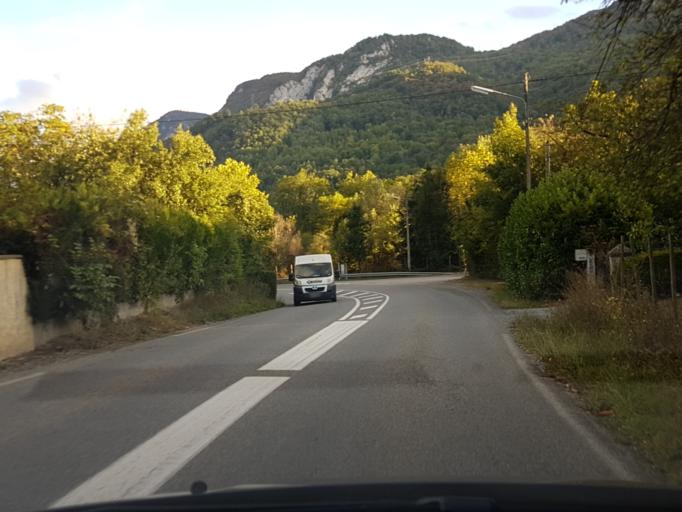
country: FR
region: Midi-Pyrenees
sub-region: Departement de l'Ariege
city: Tarascon-sur-Ariege
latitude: 42.8574
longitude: 1.5830
